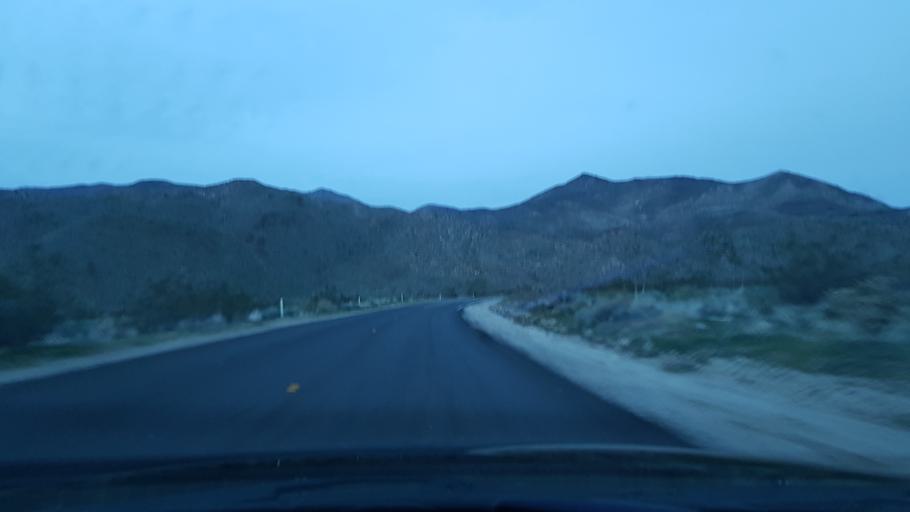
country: US
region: California
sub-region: San Diego County
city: Julian
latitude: 33.0074
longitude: -116.4562
